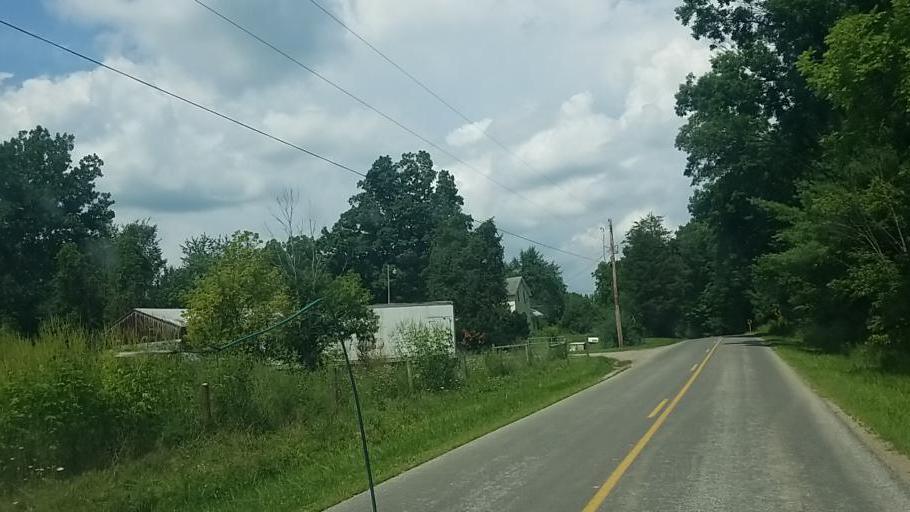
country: US
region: Ohio
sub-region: Medina County
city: Lodi
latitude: 41.0947
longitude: -82.0803
